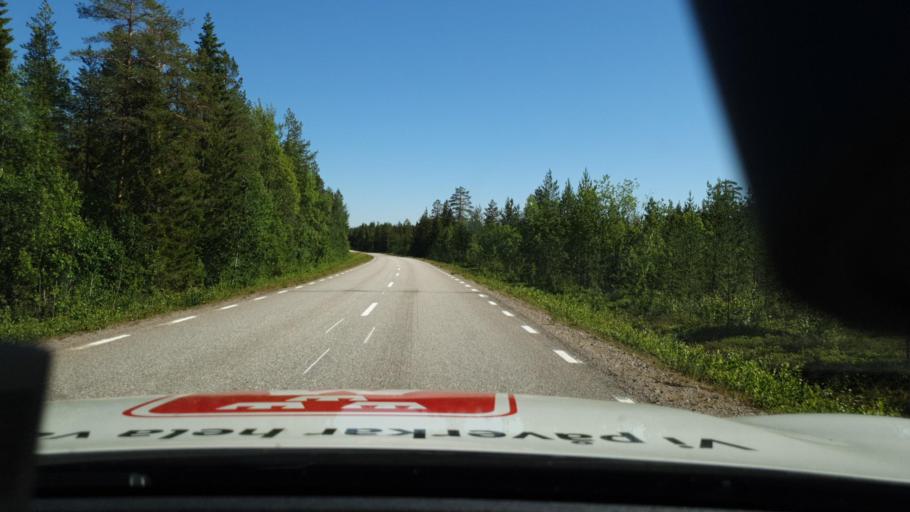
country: SE
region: Norrbotten
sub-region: Lulea Kommun
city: Ranea
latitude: 65.9888
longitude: 22.3459
